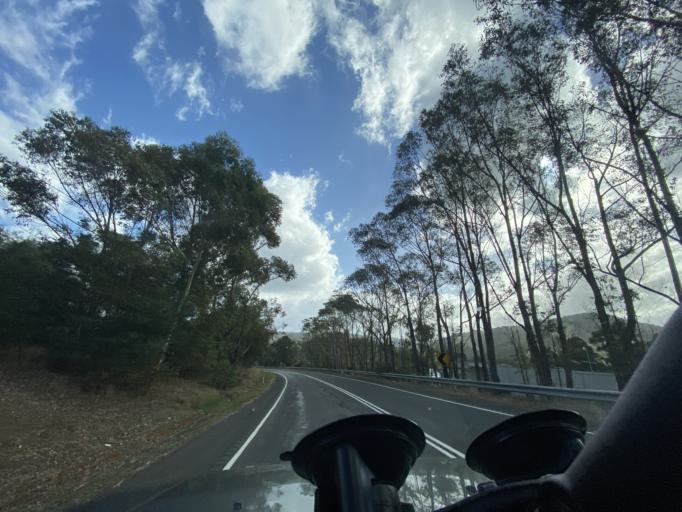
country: AU
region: Victoria
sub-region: Murrindindi
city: Kinglake West
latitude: -37.3173
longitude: 145.2916
